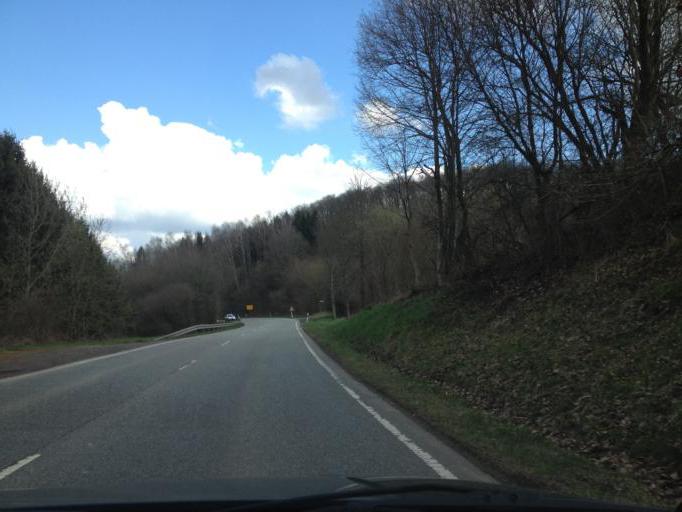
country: DE
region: Rheinland-Pfalz
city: Breitenbach
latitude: 49.4267
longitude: 7.2364
